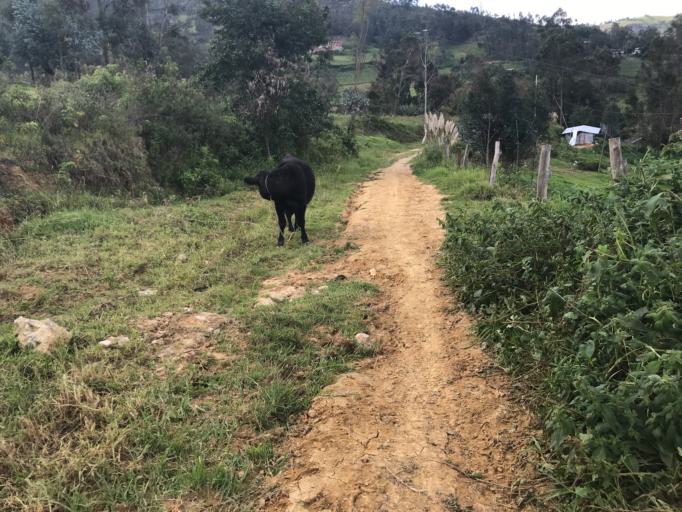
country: PE
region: Cajamarca
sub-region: Provincia de Chota
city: Querocoto
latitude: -6.3602
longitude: -79.0310
